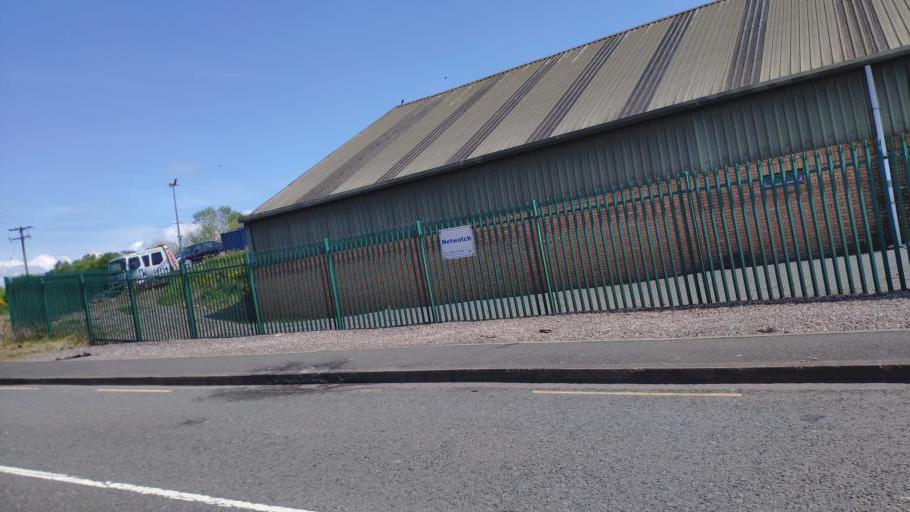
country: IE
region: Munster
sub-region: County Cork
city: Cork
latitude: 51.9282
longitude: -8.4901
